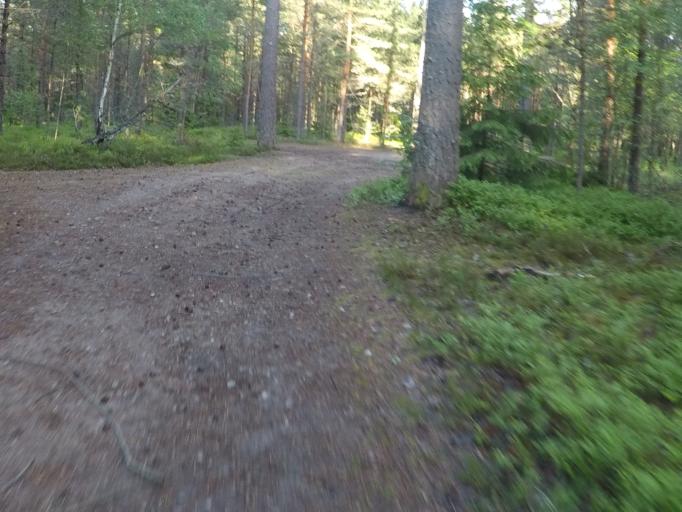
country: SE
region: Soedermanland
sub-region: Eskilstuna Kommun
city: Hallbybrunn
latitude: 59.3946
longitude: 16.3961
